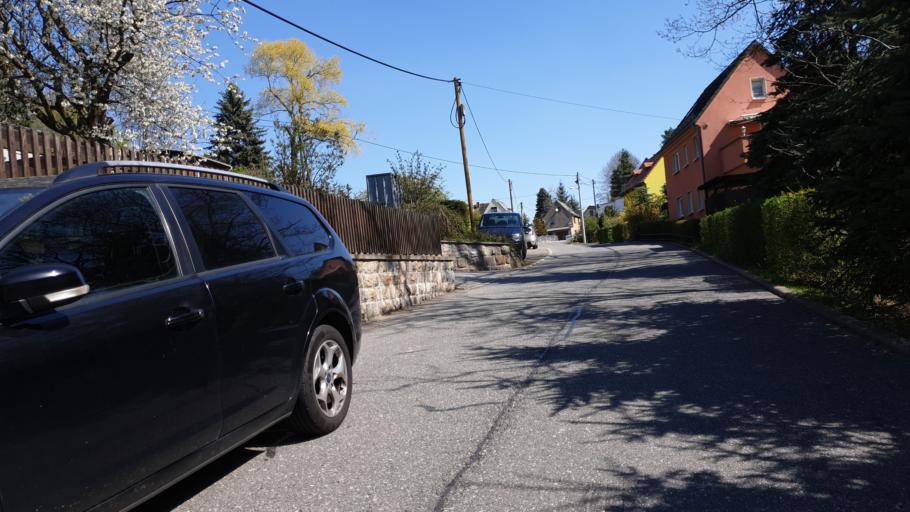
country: DE
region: Saxony
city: Taura
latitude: 50.9425
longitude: 12.8482
